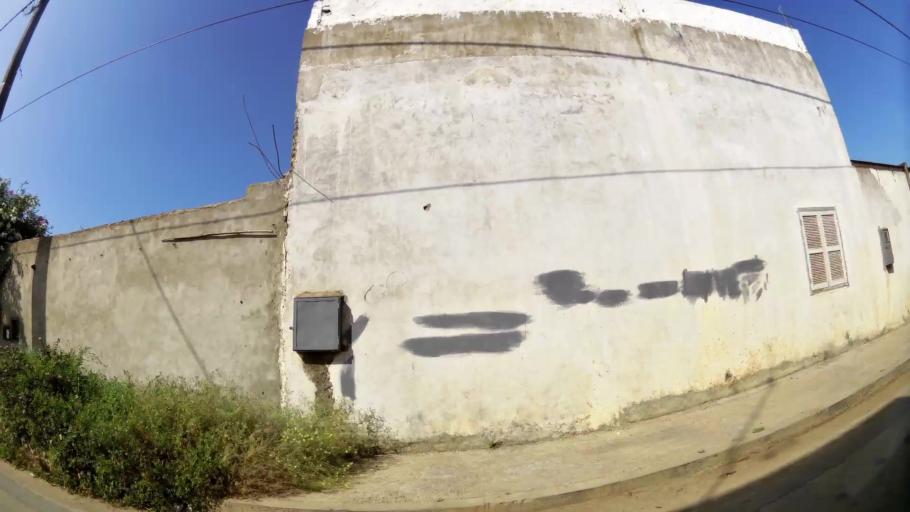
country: MA
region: Rabat-Sale-Zemmour-Zaer
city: Sale
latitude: 34.0725
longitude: -6.7608
